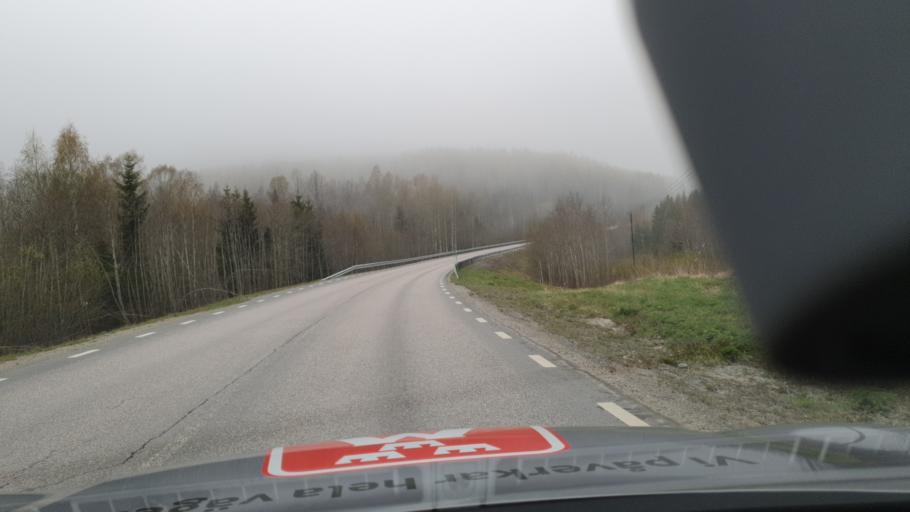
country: SE
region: Vaesternorrland
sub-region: OErnskoeldsviks Kommun
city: Ornskoldsvik
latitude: 63.3407
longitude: 18.8373
